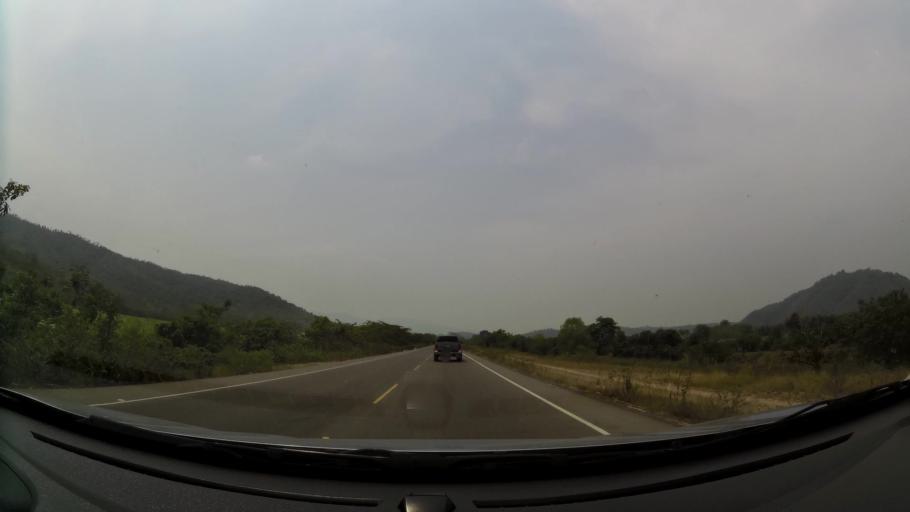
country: HN
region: Cortes
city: Potrerillos
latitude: 15.2527
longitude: -87.9560
